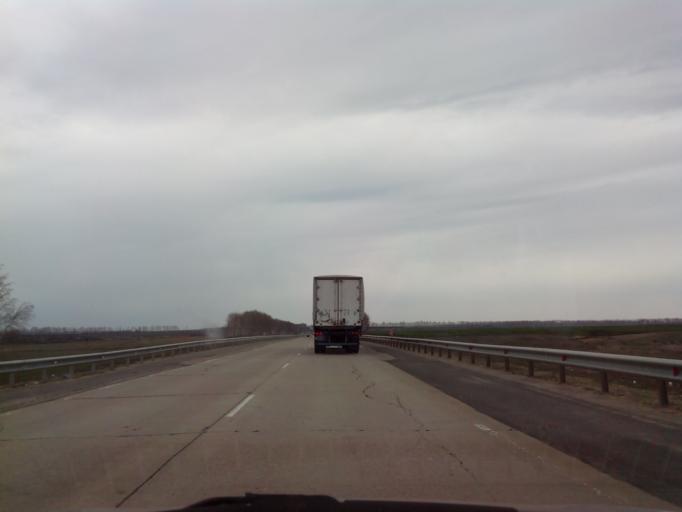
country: RU
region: Tambov
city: Pokrovo-Prigorodnoye
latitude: 52.6449
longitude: 41.3412
